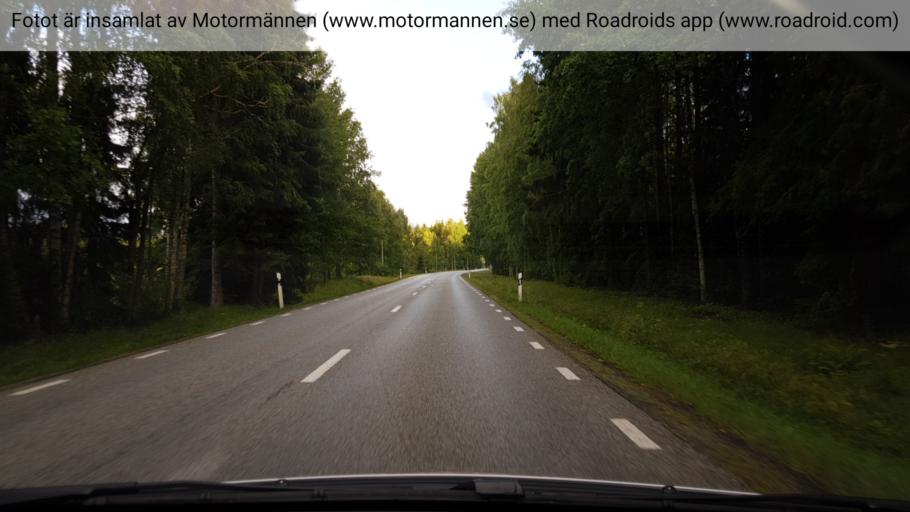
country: SE
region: OErebro
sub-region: Hallefors Kommun
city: Haellefors
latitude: 59.6201
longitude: 14.6383
